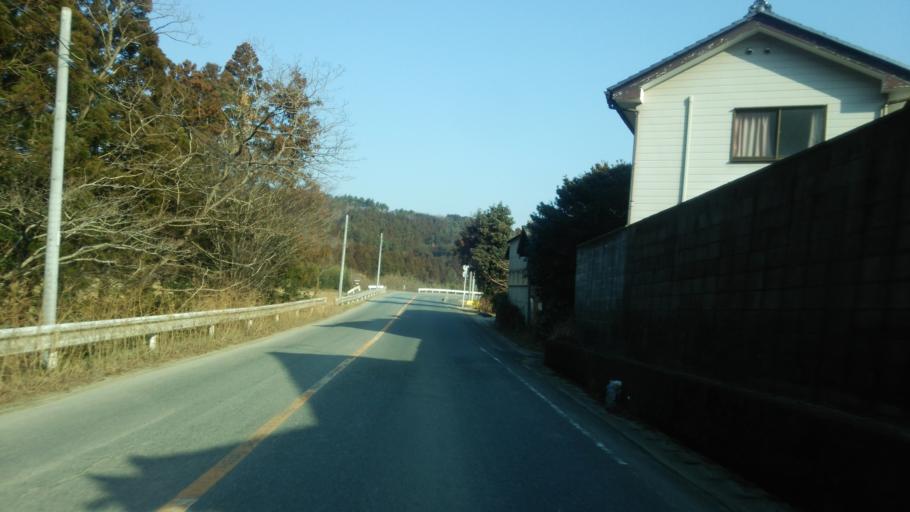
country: JP
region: Fukushima
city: Iwaki
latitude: 37.0659
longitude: 140.8054
